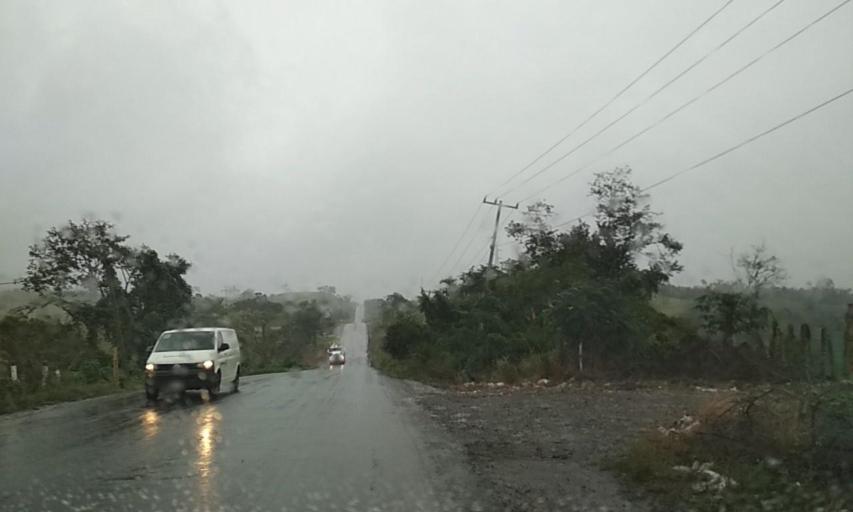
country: MX
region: Veracruz
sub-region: Papantla
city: El Chote
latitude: 20.3938
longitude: -97.3282
